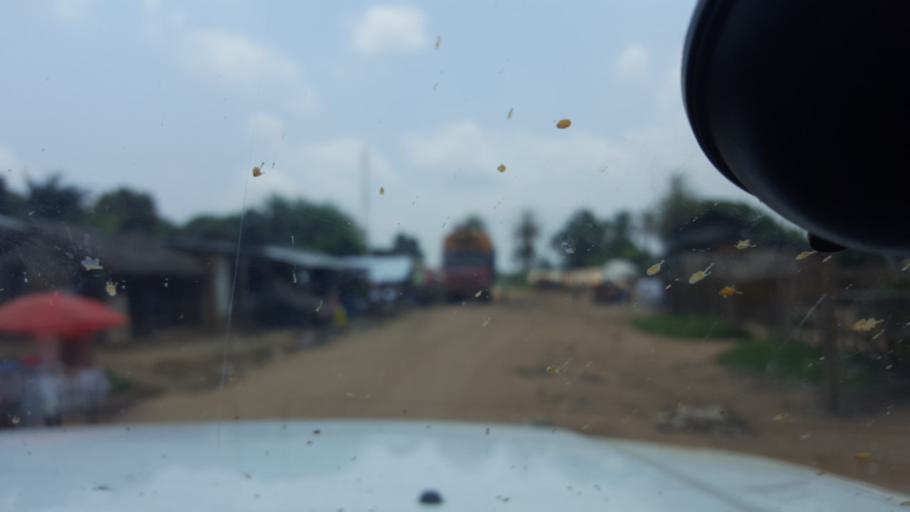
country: CD
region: Bandundu
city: Mushie
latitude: -3.7424
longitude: 16.6520
